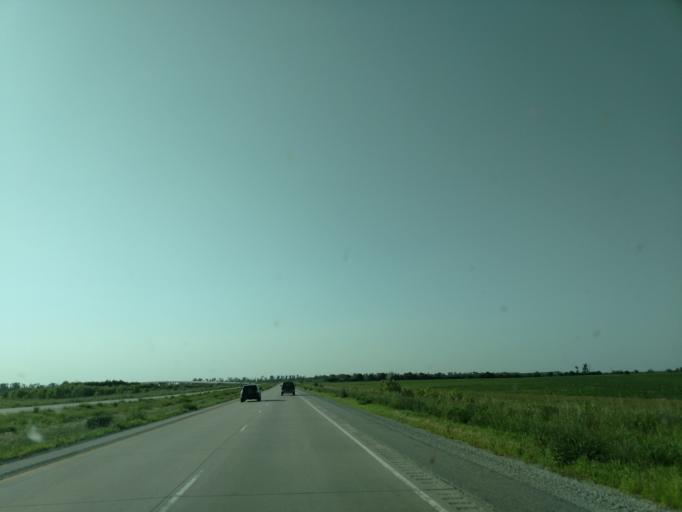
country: US
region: Nebraska
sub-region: Cass County
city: Plattsmouth
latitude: 41.0527
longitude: -95.8642
